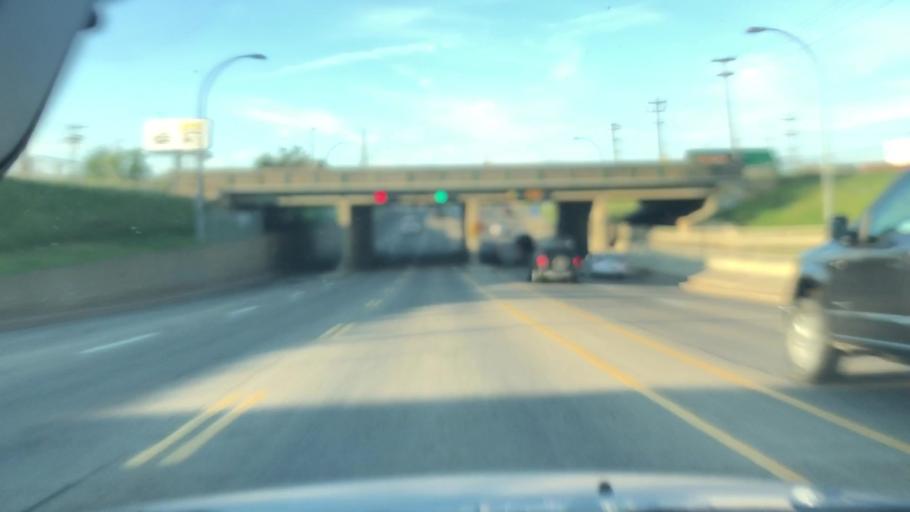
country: CA
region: Alberta
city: Edmonton
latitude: 53.5842
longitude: -113.5411
